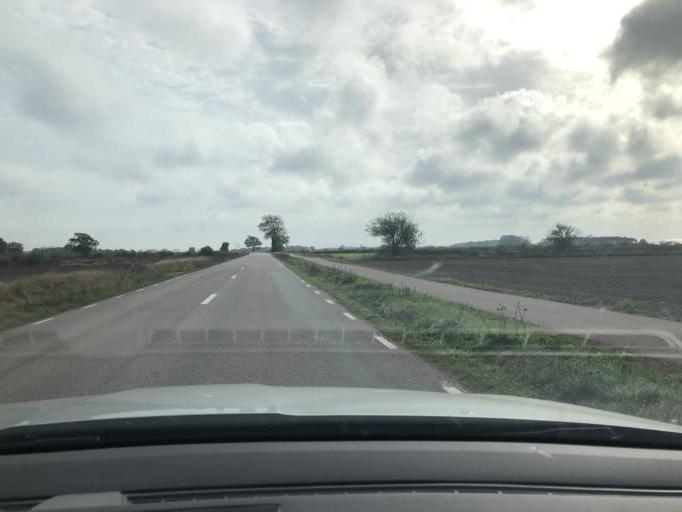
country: SE
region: Kalmar
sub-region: Morbylanga Kommun
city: Moerbylanga
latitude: 56.3135
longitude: 16.4061
